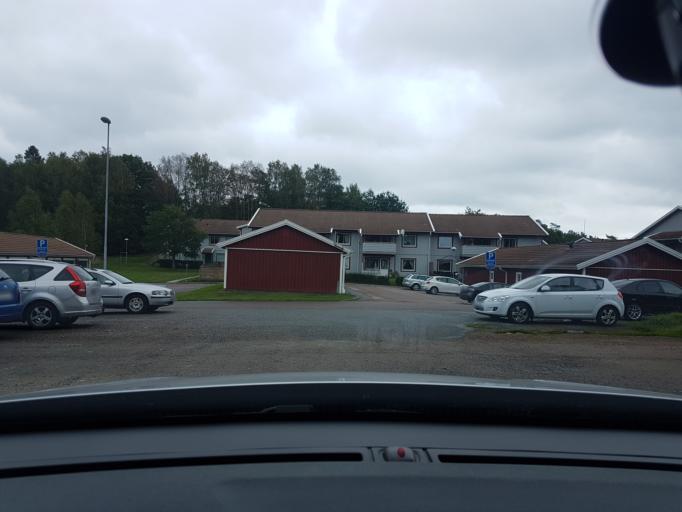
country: SE
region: Vaestra Goetaland
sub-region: Ale Kommun
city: Salanda
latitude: 57.9869
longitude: 12.2162
